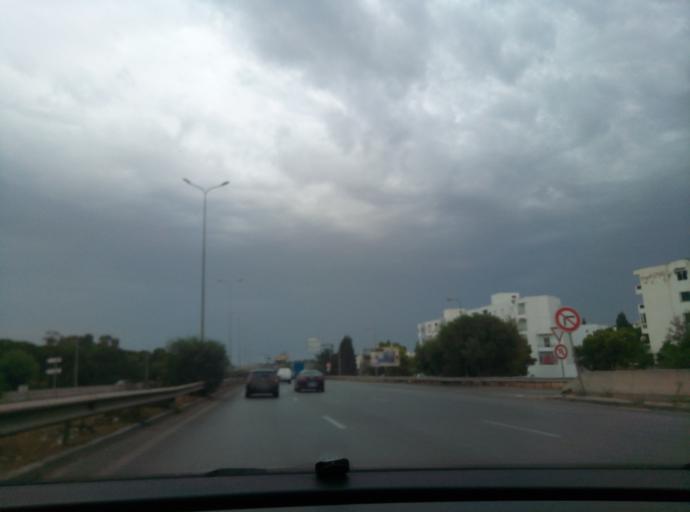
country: TN
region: Bin 'Arus
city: Ben Arous
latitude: 36.7449
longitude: 10.2113
